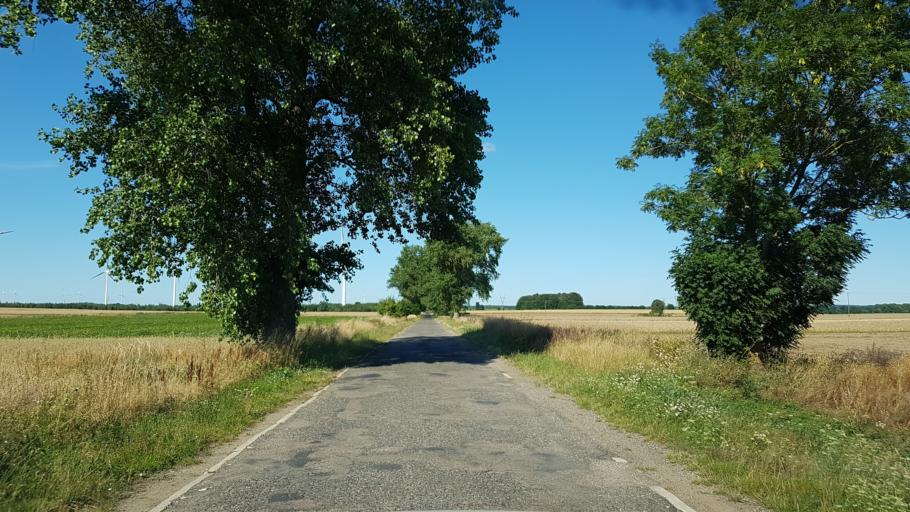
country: PL
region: West Pomeranian Voivodeship
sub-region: Powiat kamienski
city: Wolin
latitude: 53.7876
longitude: 14.6354
